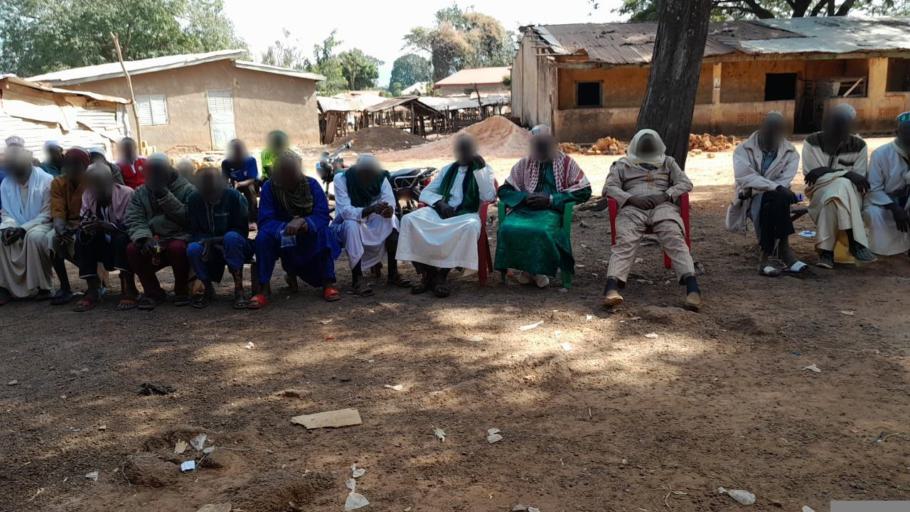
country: GN
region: Mamou
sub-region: Pita
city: Pita
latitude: 10.9502
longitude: -12.3117
